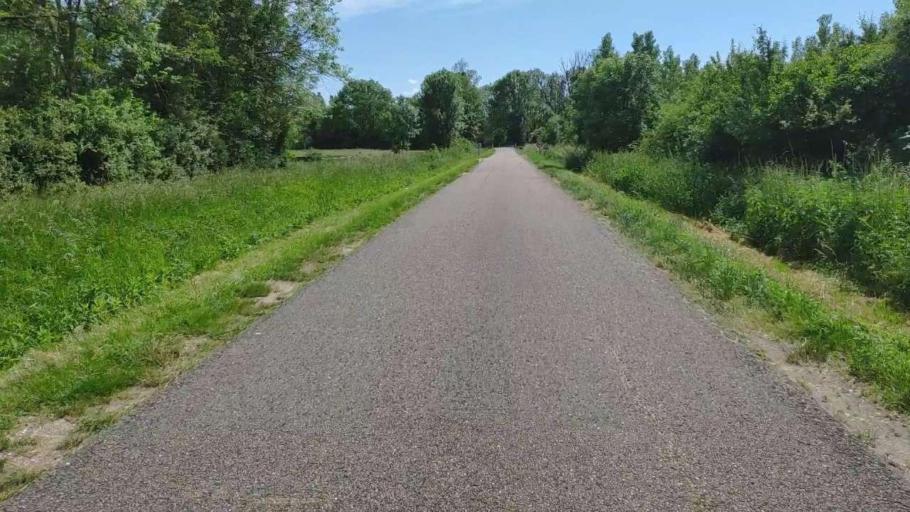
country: FR
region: Franche-Comte
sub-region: Departement du Jura
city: Bletterans
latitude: 46.7241
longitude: 5.4768
